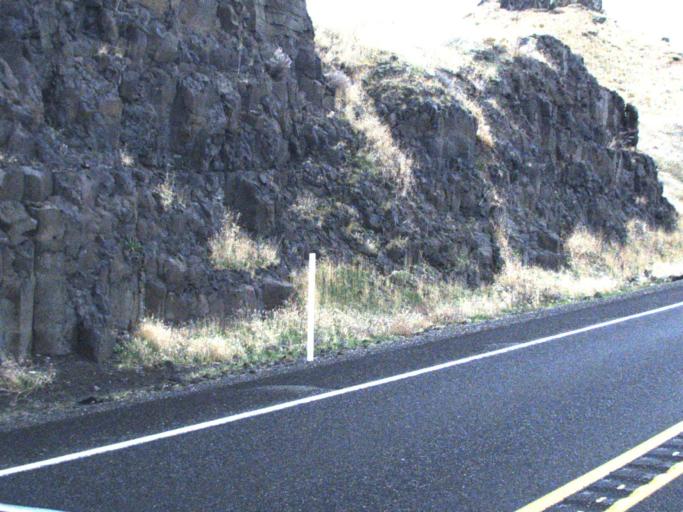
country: US
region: Washington
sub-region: Benton County
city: Finley
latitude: 46.0455
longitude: -118.9398
